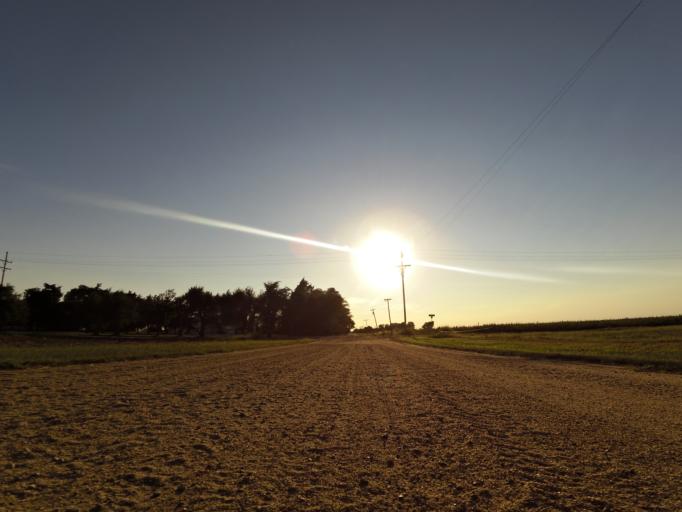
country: US
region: Kansas
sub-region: Reno County
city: South Hutchinson
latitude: 38.0137
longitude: -98.0314
